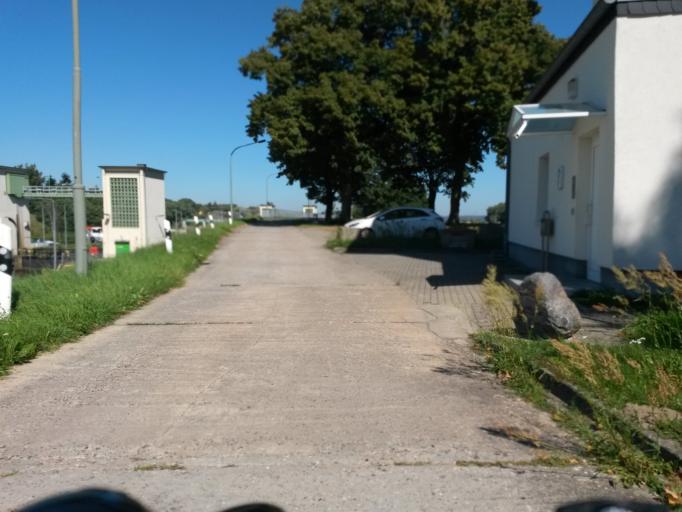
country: PL
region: West Pomeranian Voivodeship
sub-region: Powiat gryfinski
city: Cedynia
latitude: 52.8742
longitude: 14.1497
